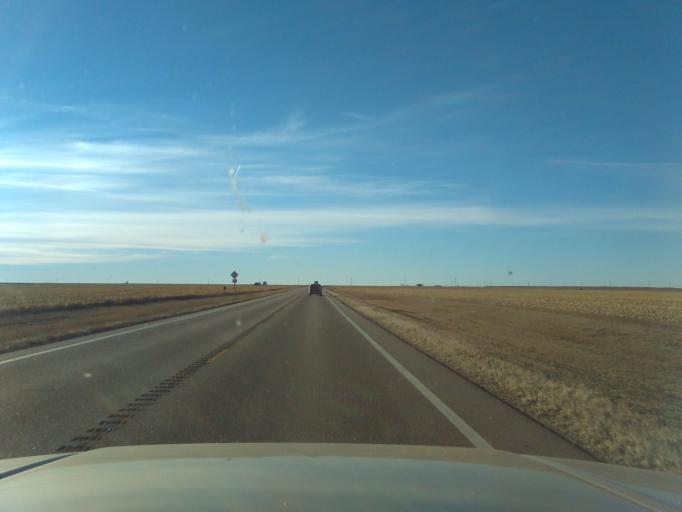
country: US
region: Kansas
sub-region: Thomas County
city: Colby
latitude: 39.4649
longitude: -100.7469
